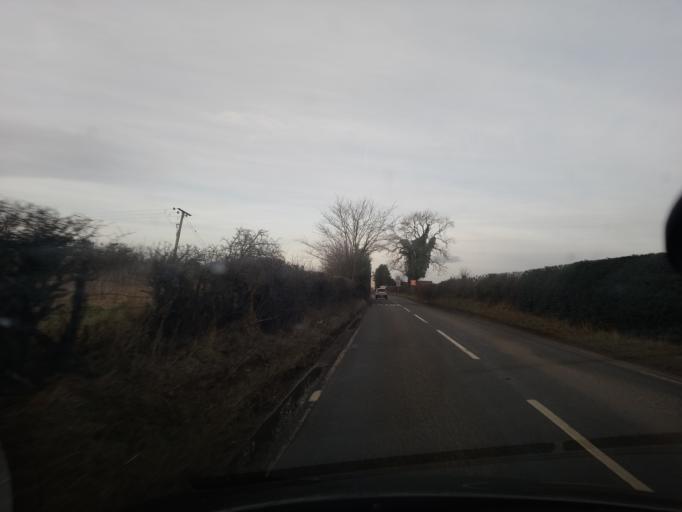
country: GB
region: England
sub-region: Shropshire
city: Wem
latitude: 52.8893
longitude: -2.7099
